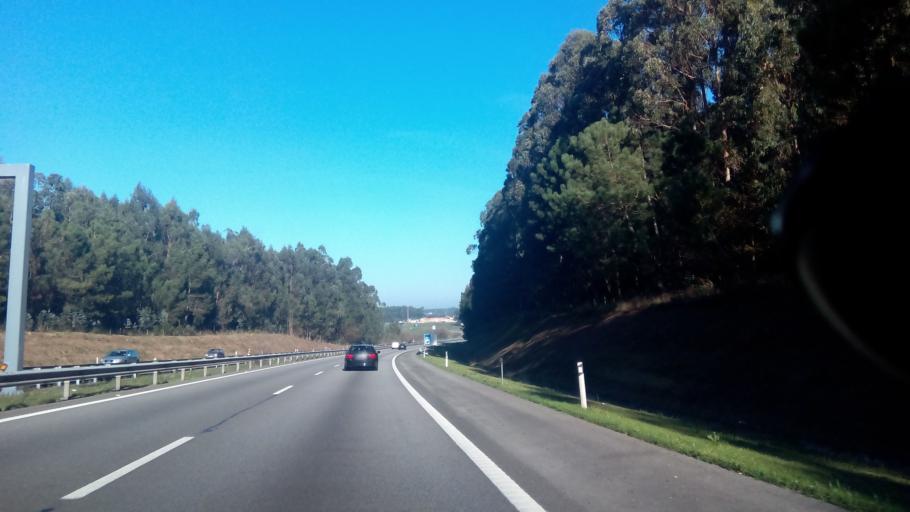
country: PT
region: Porto
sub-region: Matosinhos
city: Lavra
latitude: 41.2713
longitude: -8.7020
